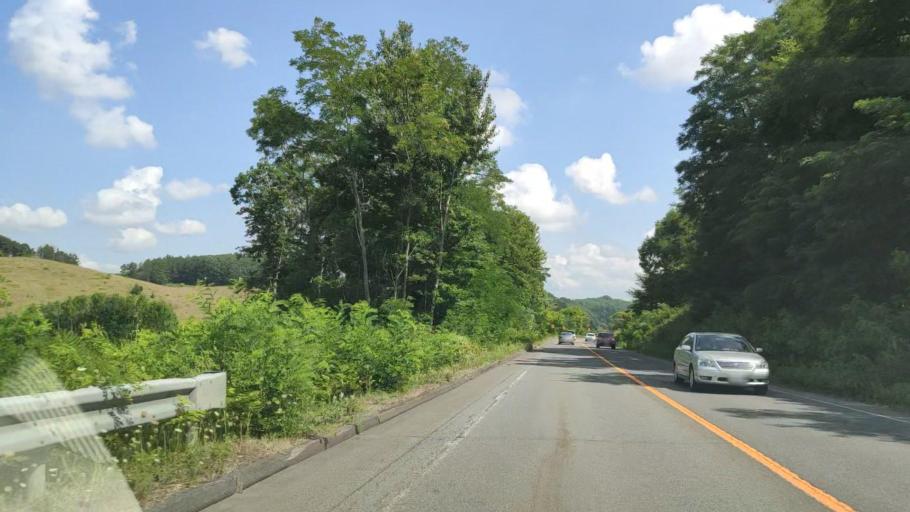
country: JP
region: Hokkaido
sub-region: Asahikawa-shi
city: Asahikawa
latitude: 43.5855
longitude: 142.4438
